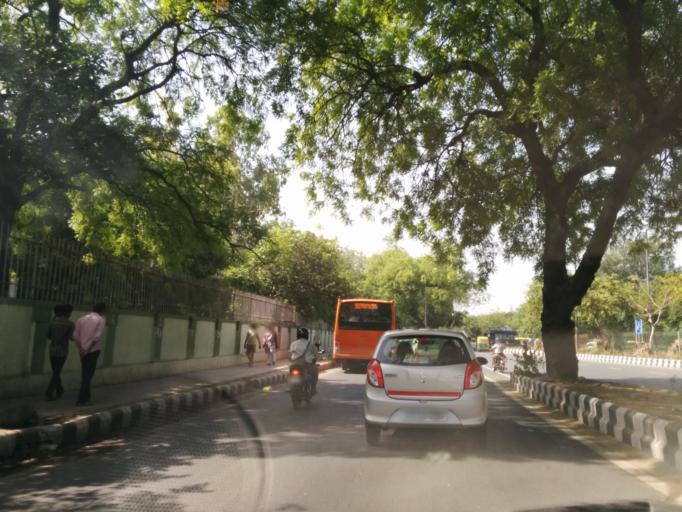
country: IN
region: NCT
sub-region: New Delhi
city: New Delhi
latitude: 28.5657
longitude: 77.2077
